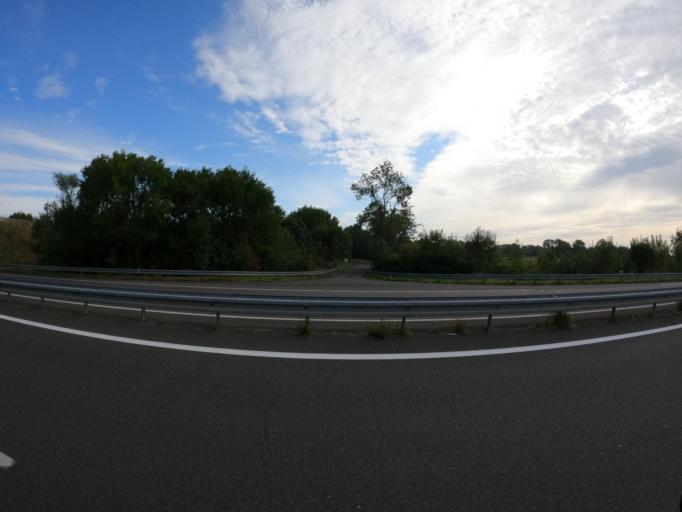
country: FR
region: Centre
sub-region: Departement d'Indre-et-Loire
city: Saint-Nicolas-de-Bourgueil
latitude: 47.2714
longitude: 0.1104
